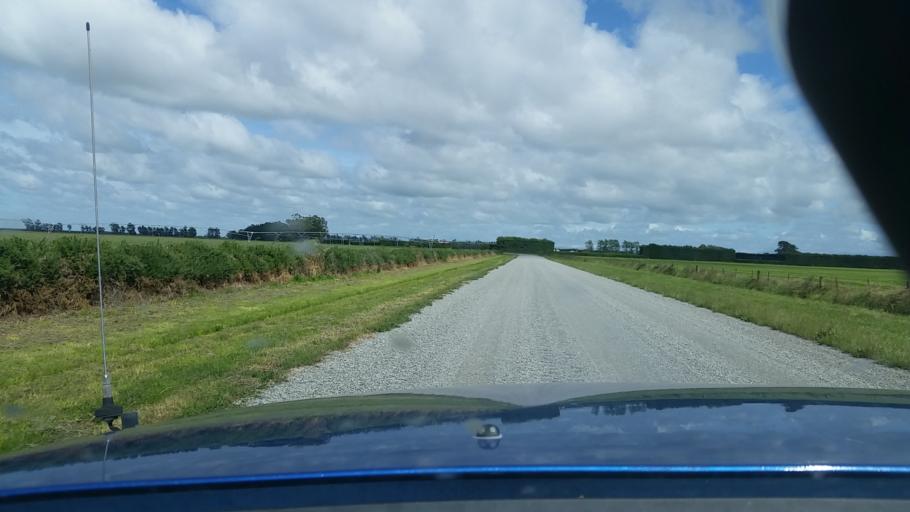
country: NZ
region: Canterbury
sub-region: Ashburton District
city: Rakaia
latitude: -43.8358
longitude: 171.9752
